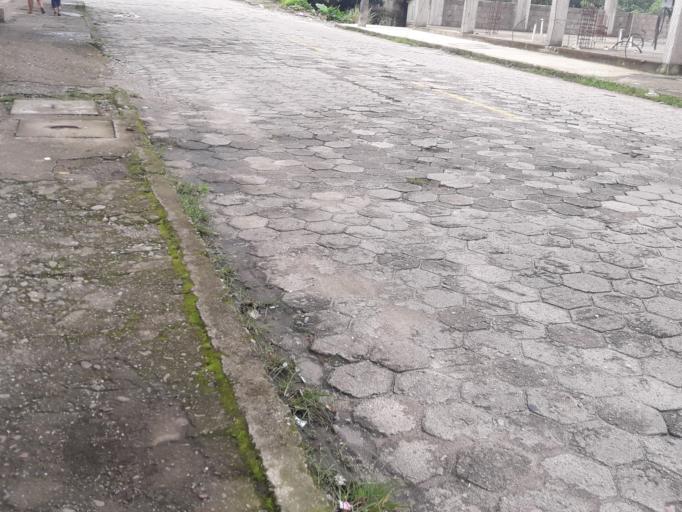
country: EC
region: Napo
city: Tena
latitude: -0.9963
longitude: -77.8147
